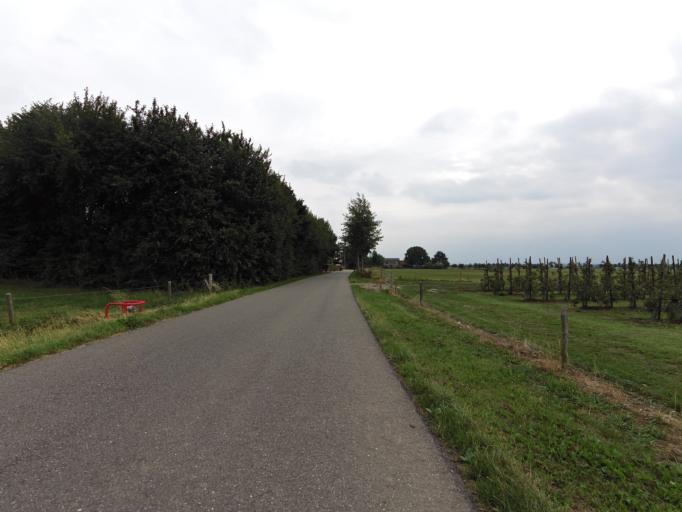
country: NL
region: Gelderland
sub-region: Gemeente Zevenaar
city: Zevenaar
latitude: 51.8600
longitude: 6.0354
